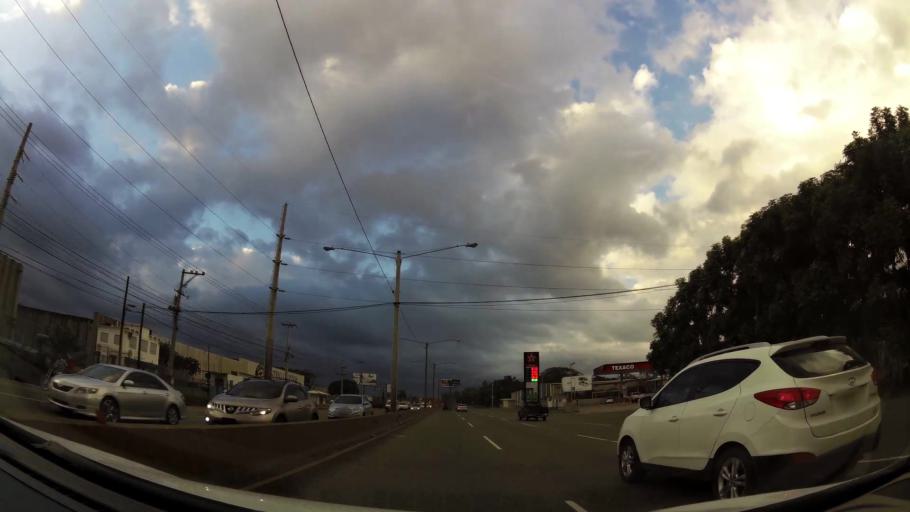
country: DO
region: Santo Domingo
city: Santo Domingo Oeste
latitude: 18.5292
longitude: -70.0113
